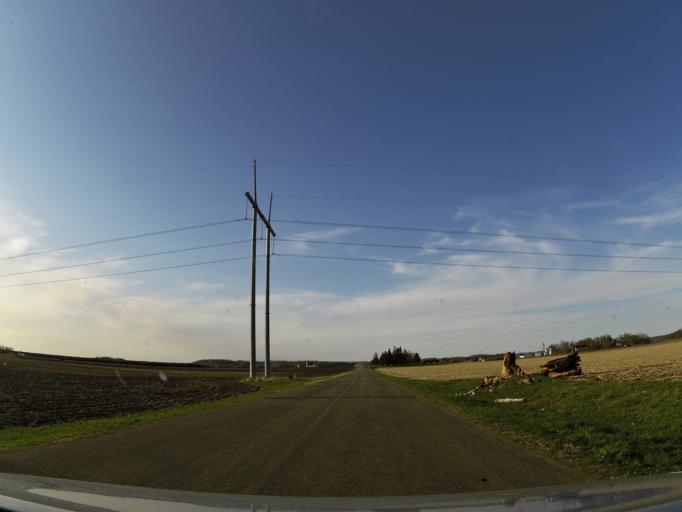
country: US
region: Minnesota
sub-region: Washington County
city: Afton
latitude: 44.8551
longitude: -92.7159
